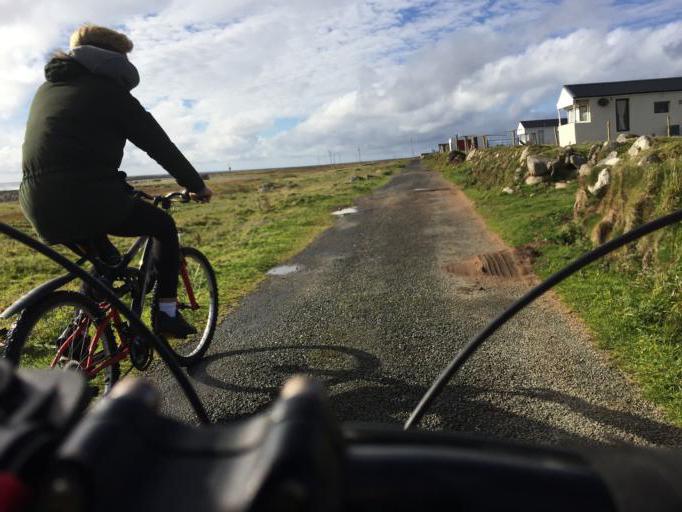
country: IE
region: Ulster
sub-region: County Donegal
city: Derrybeg
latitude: 55.2641
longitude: -8.2371
